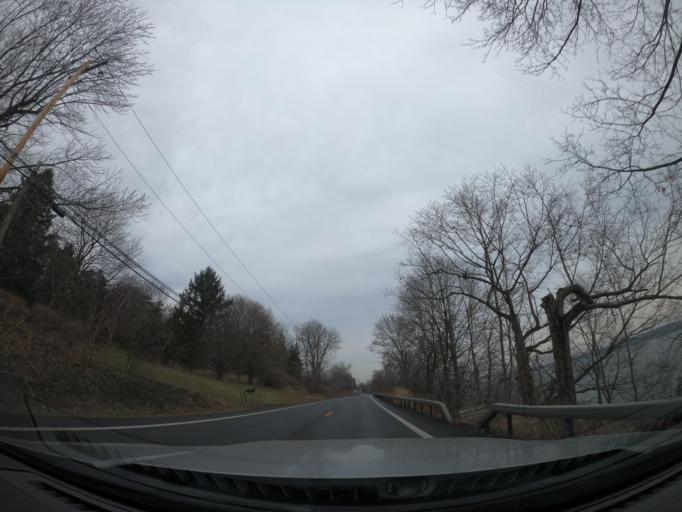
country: US
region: New York
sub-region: Cayuga County
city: Melrose Park
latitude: 42.8515
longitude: -76.5300
